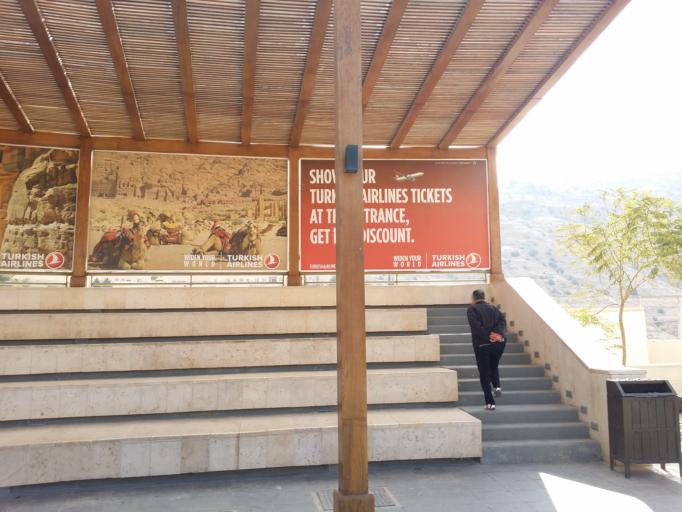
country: JO
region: Ma'an
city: Petra
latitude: 30.3245
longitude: 35.4680
